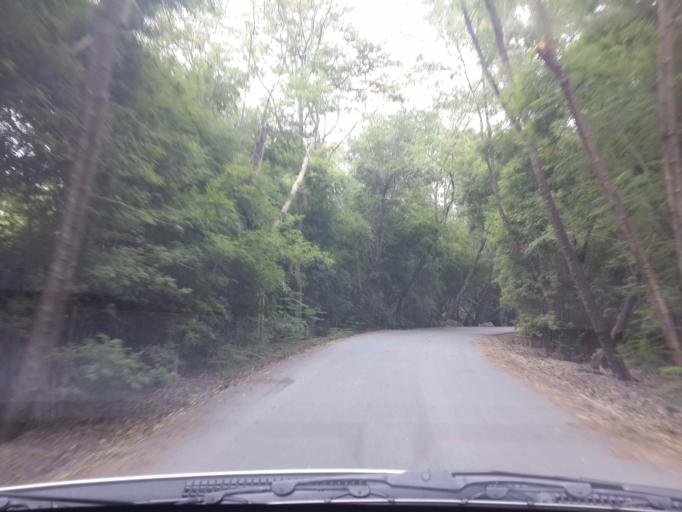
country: TH
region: Bangkok
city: Khlong Sam Wa
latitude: 13.8690
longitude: 100.7012
